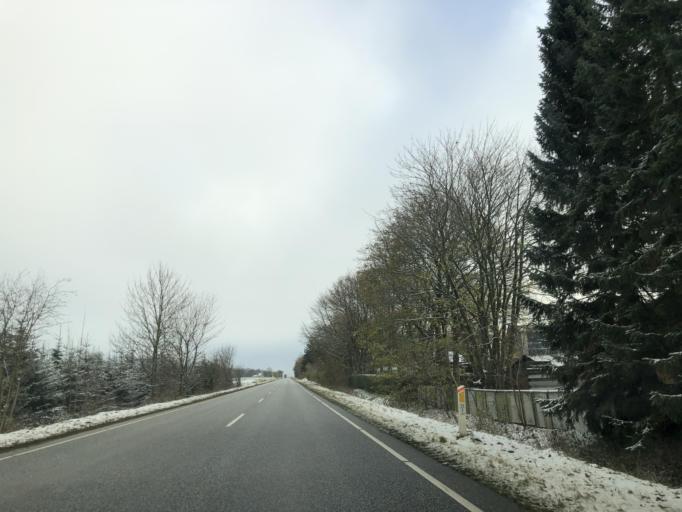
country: DK
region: Central Jutland
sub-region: Horsens Kommune
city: Braedstrup
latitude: 55.8933
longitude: 9.6507
